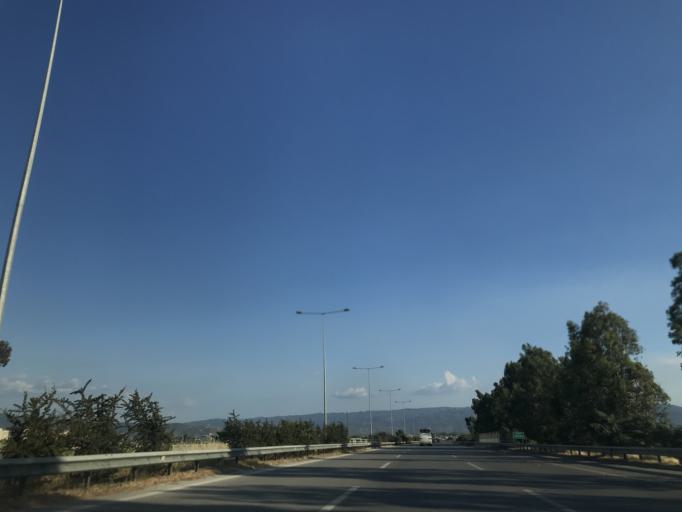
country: TR
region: Aydin
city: Aydin
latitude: 37.8380
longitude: 27.8096
